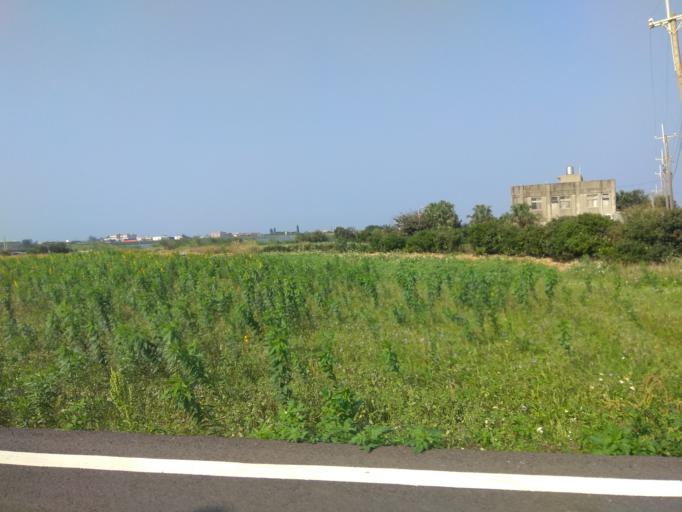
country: TW
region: Taiwan
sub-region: Hsinchu
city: Zhubei
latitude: 24.9995
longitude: 121.0445
